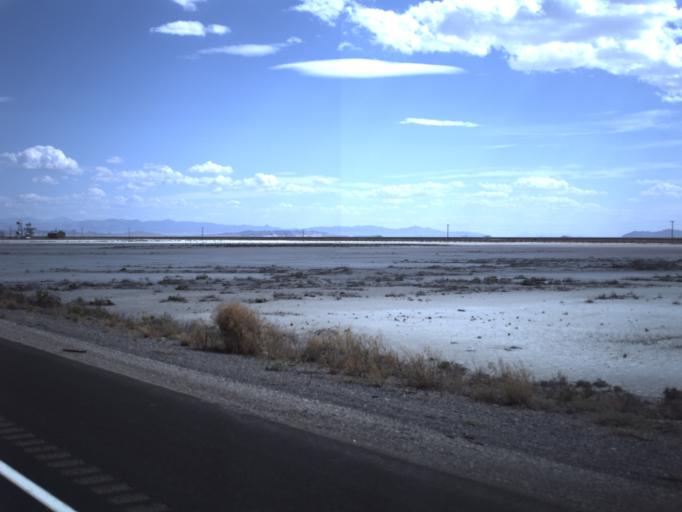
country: US
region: Utah
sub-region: Tooele County
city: Wendover
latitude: 40.7308
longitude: -113.4947
